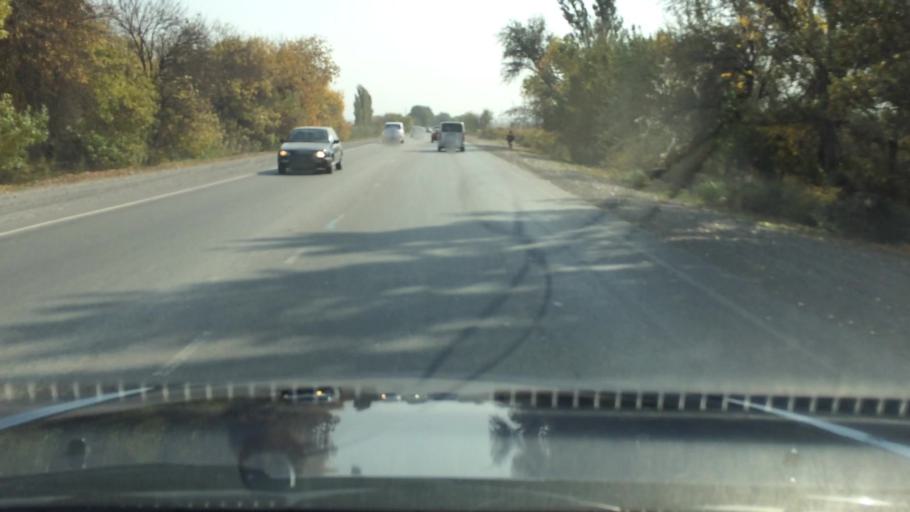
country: KG
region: Chuy
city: Lebedinovka
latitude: 42.9265
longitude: 74.6986
